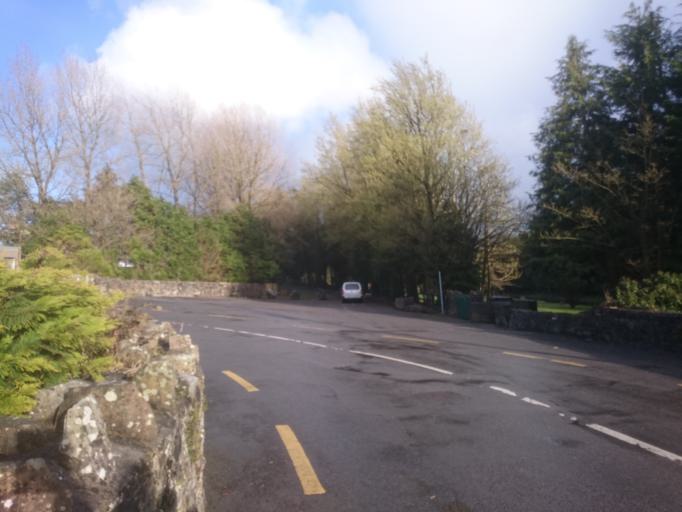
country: IE
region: Connaught
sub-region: Roscommon
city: Castlerea
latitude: 53.7696
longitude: -8.4891
